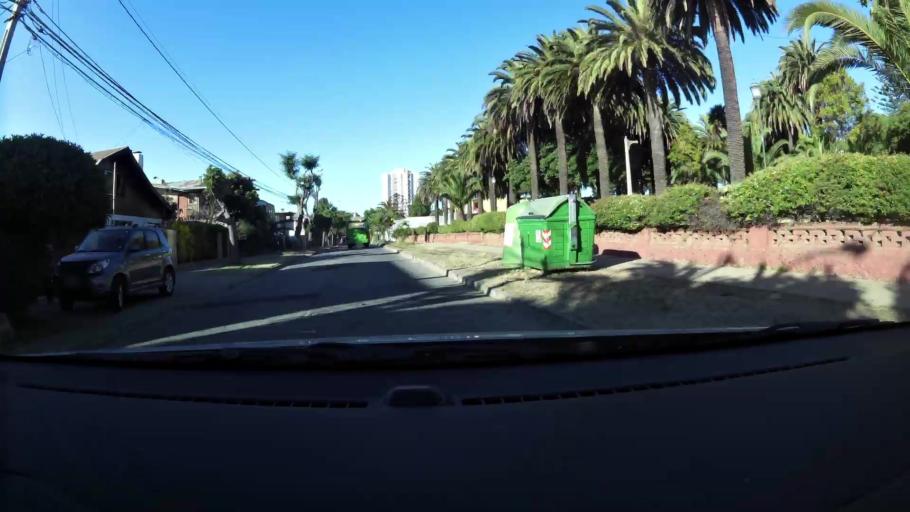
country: CL
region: Valparaiso
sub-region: Provincia de Valparaiso
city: Vina del Mar
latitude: -33.0315
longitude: -71.5818
